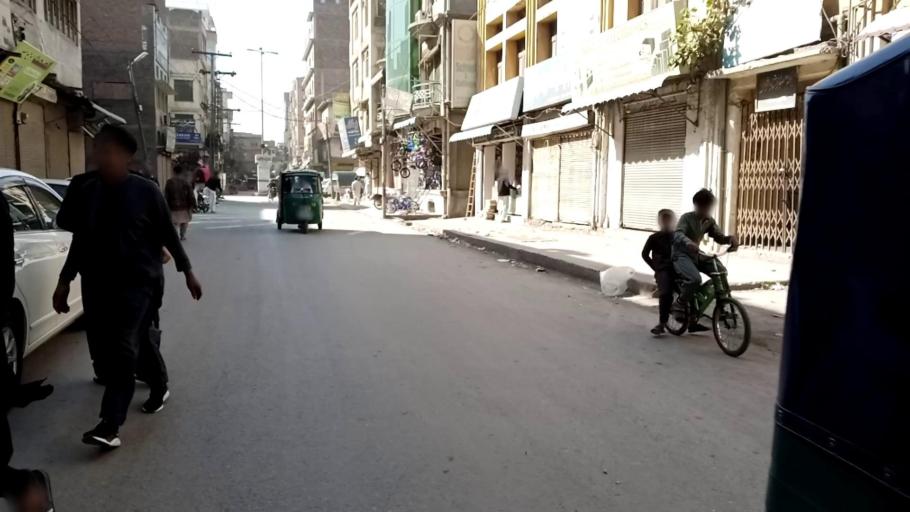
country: PK
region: Khyber Pakhtunkhwa
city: Peshawar
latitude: 34.0146
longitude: 71.5827
